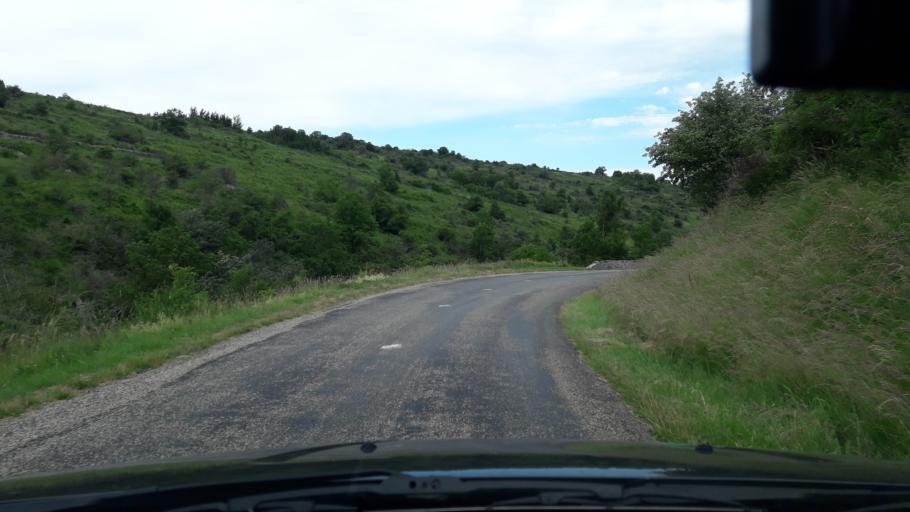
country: FR
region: Rhone-Alpes
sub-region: Departement de l'Ardeche
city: Saint-Priest
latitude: 44.6718
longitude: 4.5338
